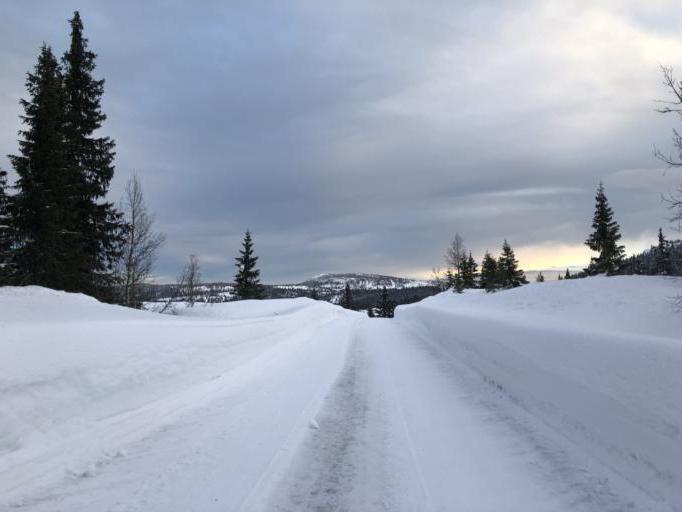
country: NO
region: Oppland
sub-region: Gausdal
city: Segalstad bru
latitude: 61.3304
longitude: 10.0523
